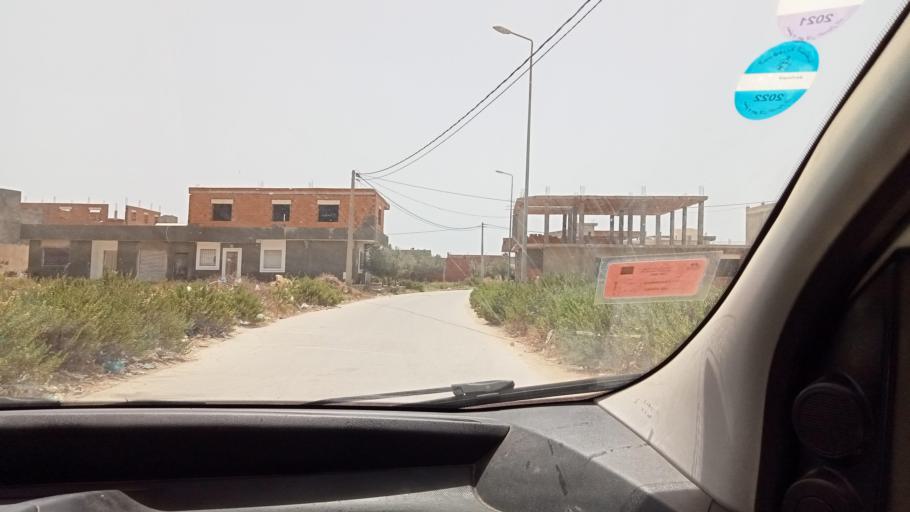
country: TN
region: Nabul
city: Qulaybiyah
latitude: 36.8582
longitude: 11.0861
